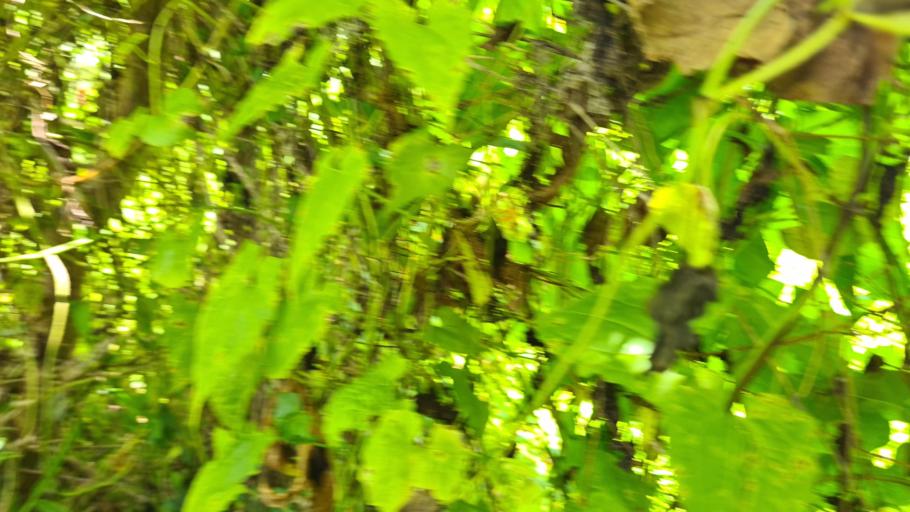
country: VU
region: Penama
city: Saratamata
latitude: -15.7660
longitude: 168.1465
